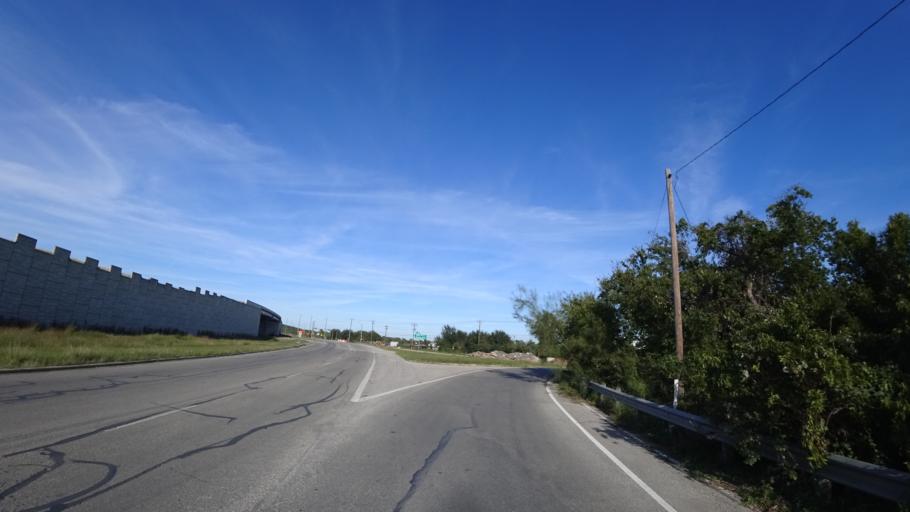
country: US
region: Texas
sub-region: Travis County
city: Austin
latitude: 30.2520
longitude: -97.6803
